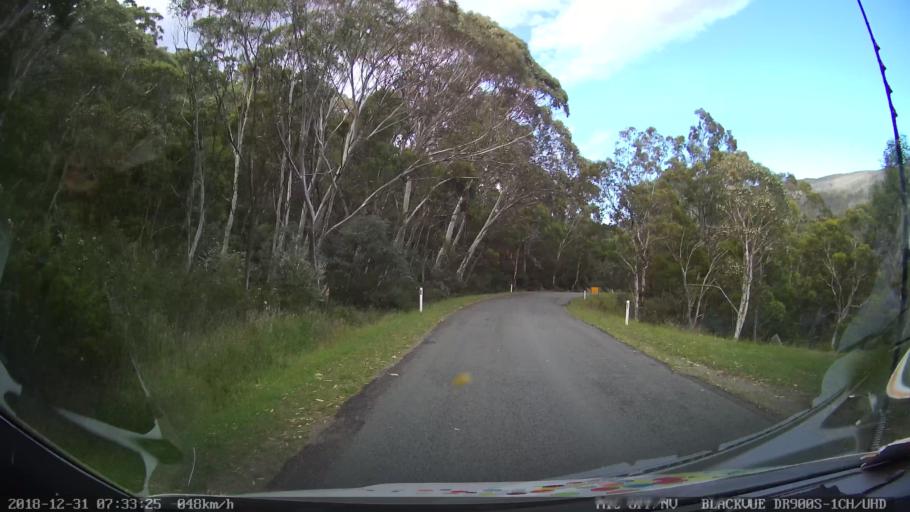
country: AU
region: New South Wales
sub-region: Snowy River
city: Jindabyne
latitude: -36.3327
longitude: 148.4573
